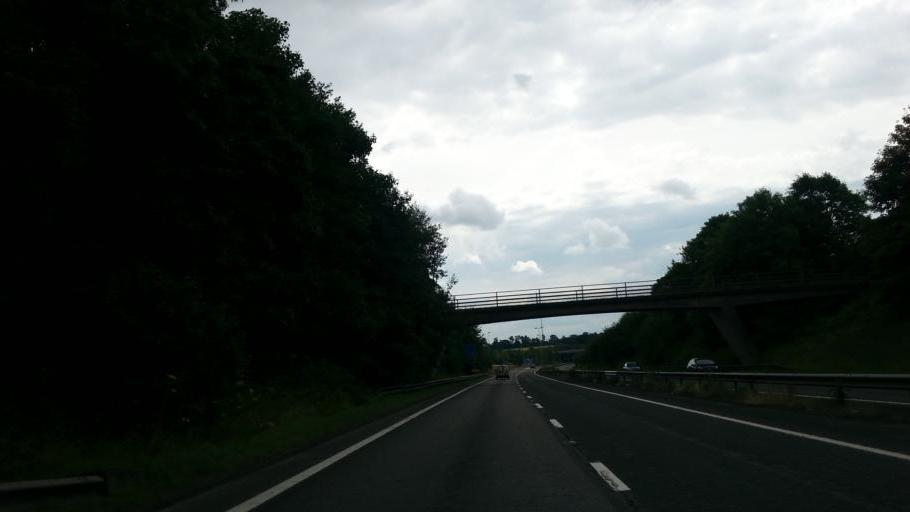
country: GB
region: England
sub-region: City and Borough of Birmingham
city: Sutton Coldfield
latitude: 52.5730
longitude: -1.7728
